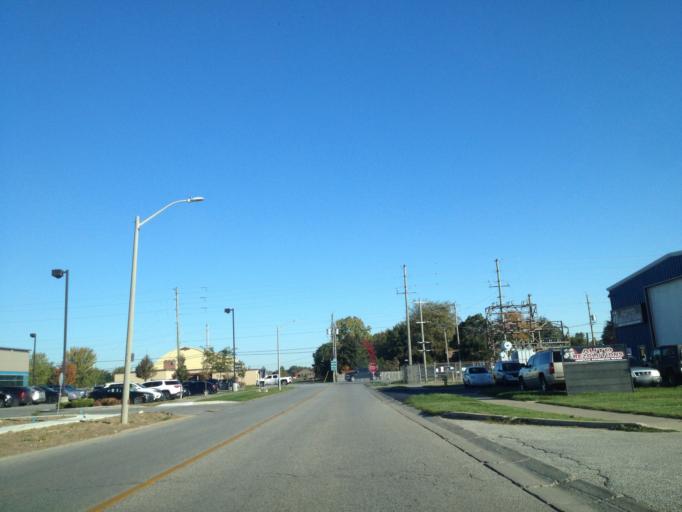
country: CA
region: Ontario
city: Amherstburg
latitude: 42.0326
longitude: -82.5936
